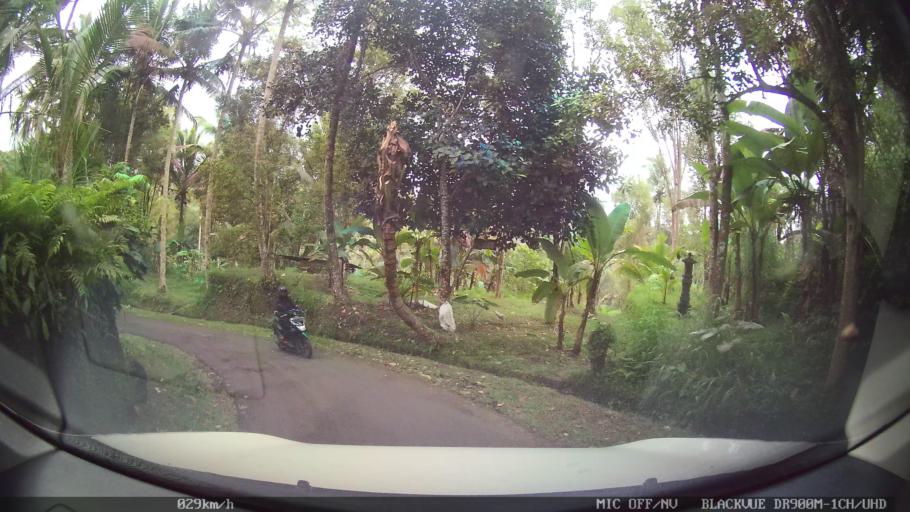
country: ID
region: Bali
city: Banjar Wangsian
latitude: -8.4584
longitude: 115.4109
